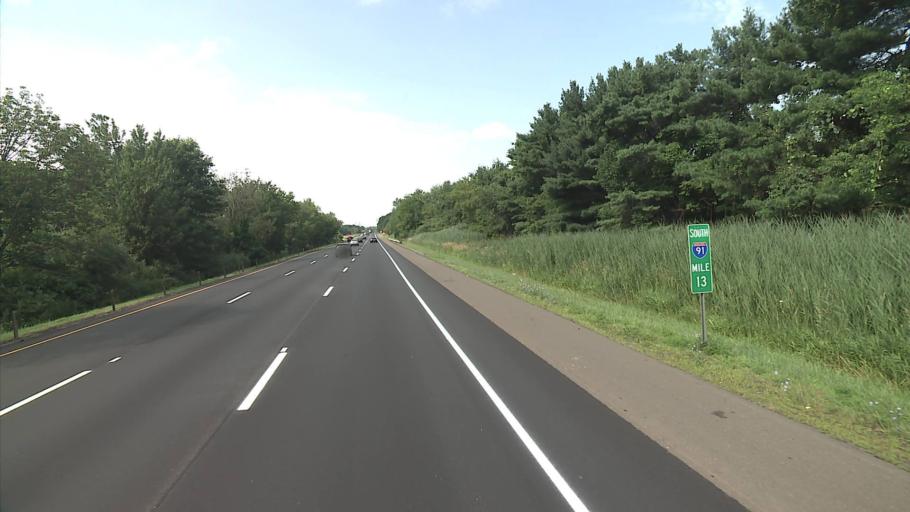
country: US
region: Connecticut
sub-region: New Haven County
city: Wallingford Center
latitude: 41.4440
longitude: -72.7916
